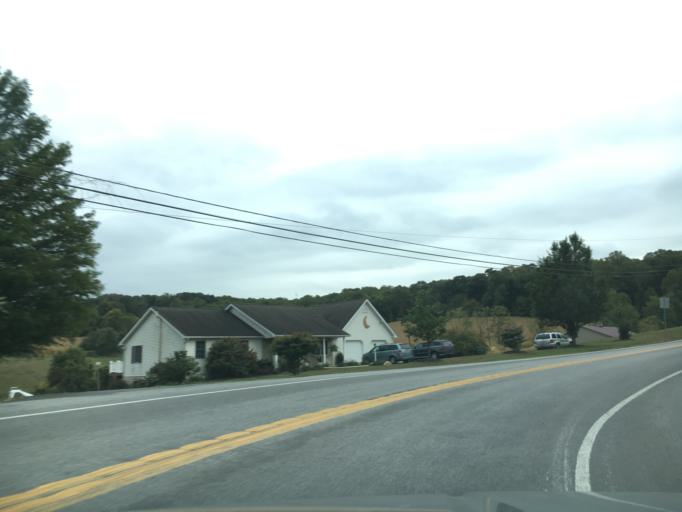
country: US
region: Pennsylvania
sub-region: Lancaster County
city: Quarryville
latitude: 39.8880
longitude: -76.1874
